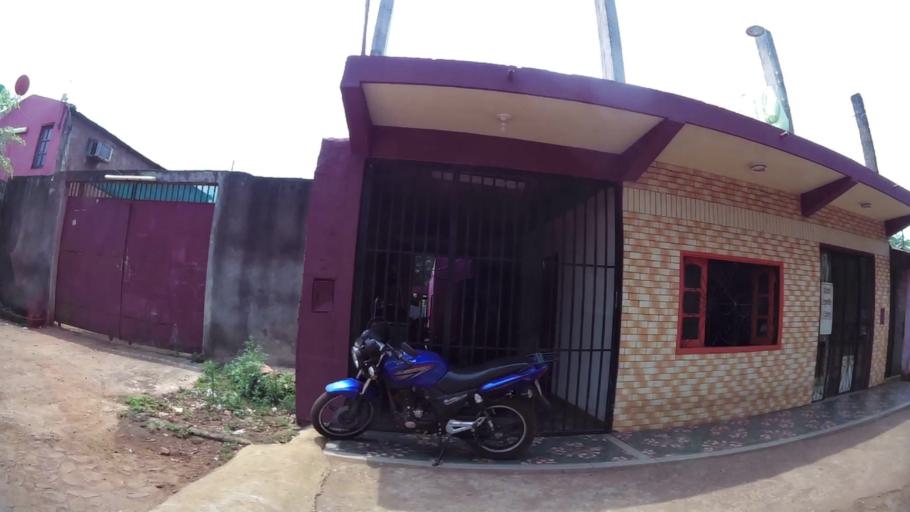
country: PY
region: Alto Parana
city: Ciudad del Este
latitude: -25.4988
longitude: -54.6294
